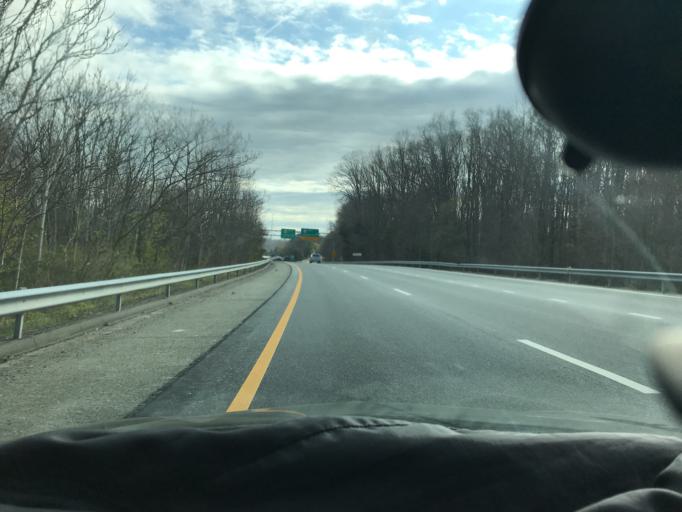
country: US
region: Virginia
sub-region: Chesterfield County
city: Bon Air
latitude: 37.5230
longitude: -77.5325
